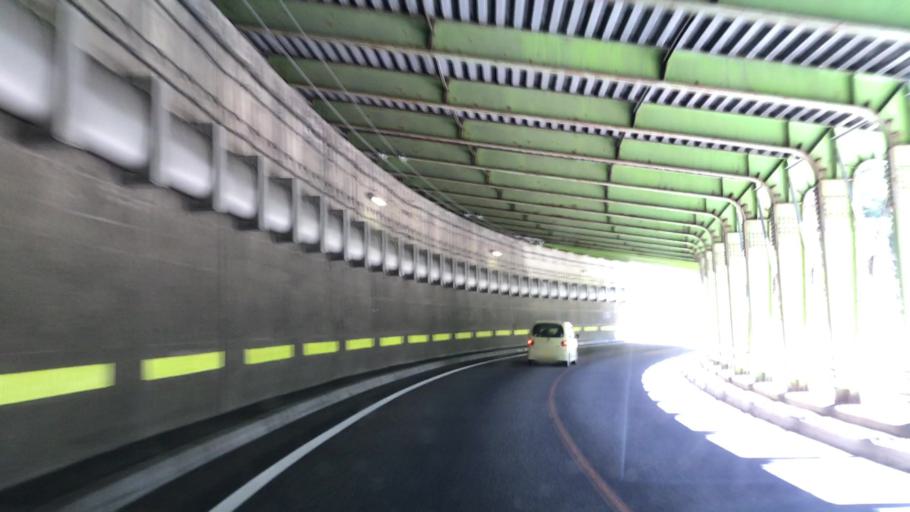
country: JP
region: Hokkaido
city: Shimo-furano
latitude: 42.9410
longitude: 142.6010
